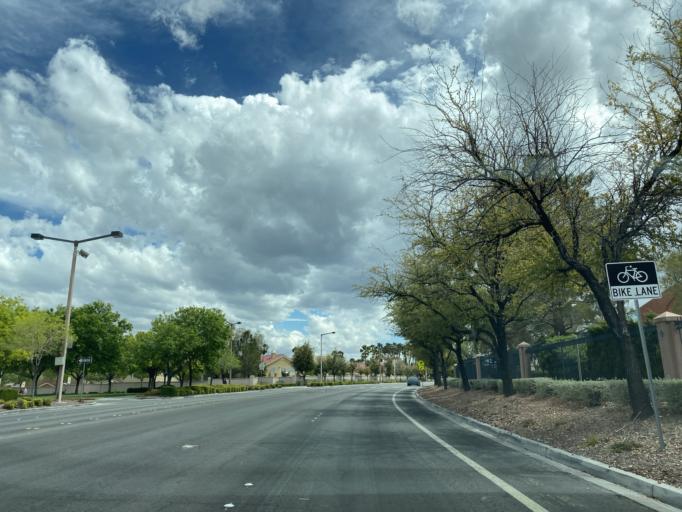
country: US
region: Nevada
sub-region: Clark County
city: Summerlin South
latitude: 36.1990
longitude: -115.2914
